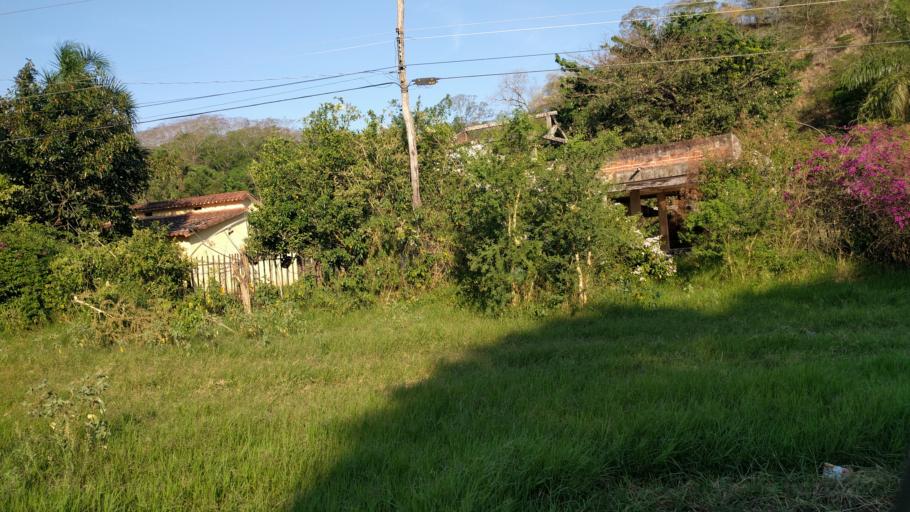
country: BO
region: Santa Cruz
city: Jorochito
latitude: -18.0836
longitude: -63.4498
